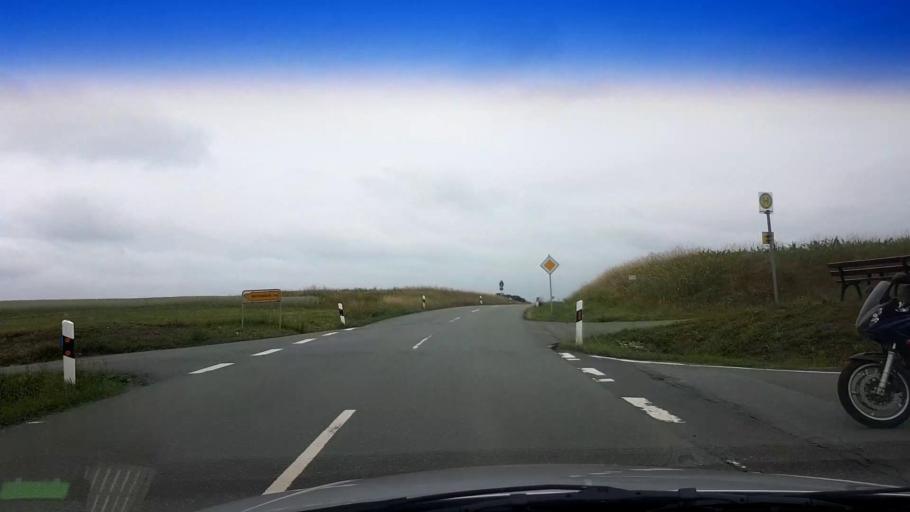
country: DE
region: Bavaria
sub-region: Upper Franconia
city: Mainleus
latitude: 50.0909
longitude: 11.3493
